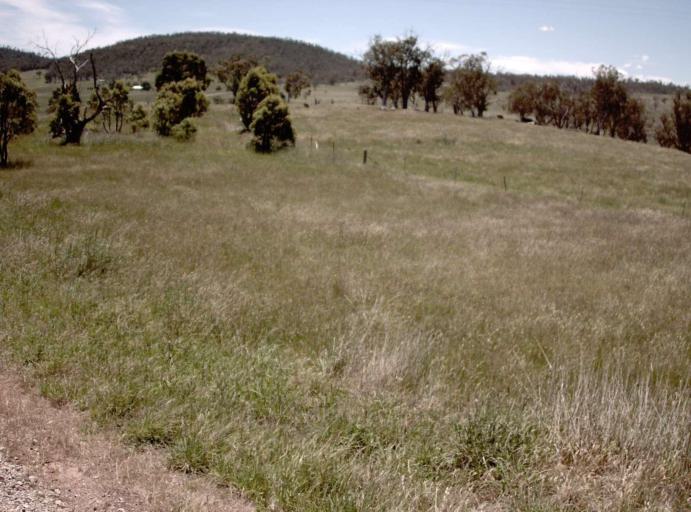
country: AU
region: New South Wales
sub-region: Snowy River
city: Jindabyne
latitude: -37.0161
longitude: 148.2747
